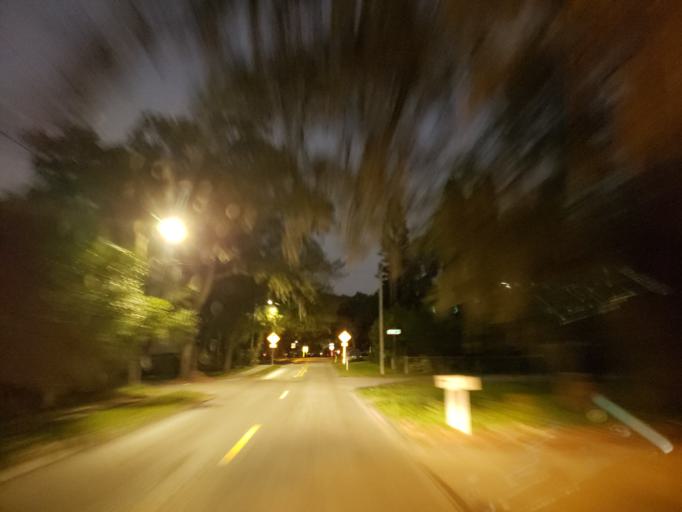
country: US
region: Florida
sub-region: Hillsborough County
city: University
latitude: 28.0226
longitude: -82.4379
